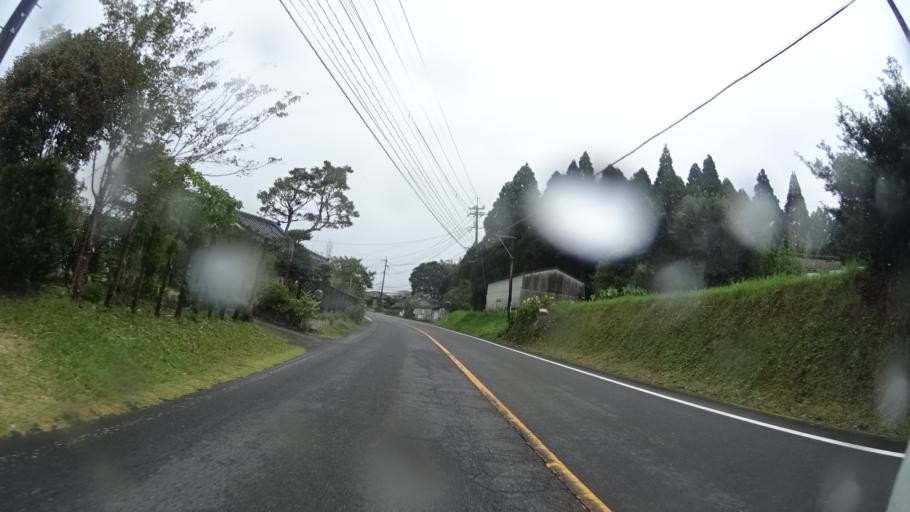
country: JP
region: Kagoshima
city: Kajiki
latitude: 31.8041
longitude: 130.6758
